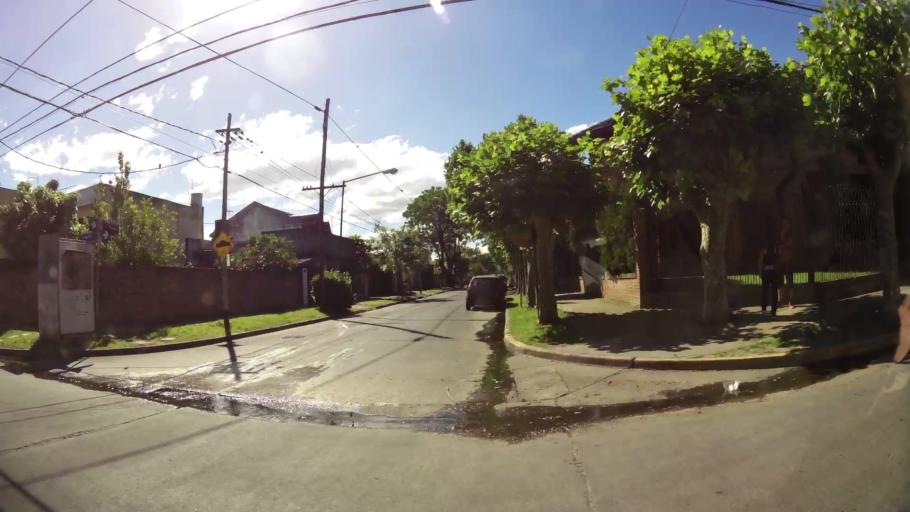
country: AR
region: Buenos Aires
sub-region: Partido de San Isidro
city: San Isidro
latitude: -34.5103
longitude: -58.5741
